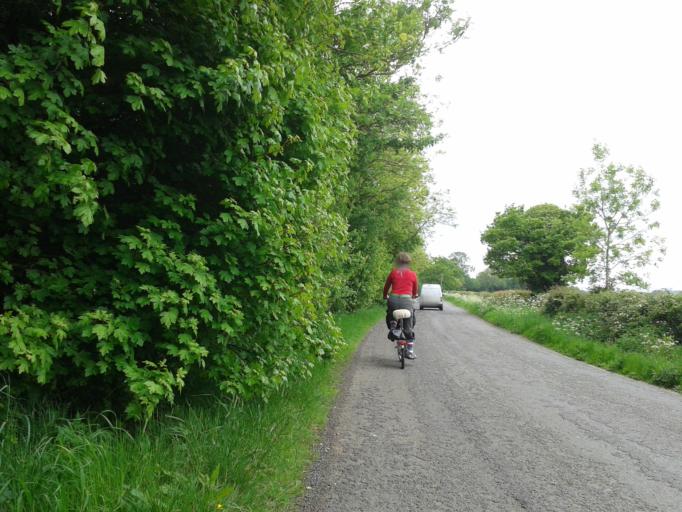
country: GB
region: England
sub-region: Northamptonshire
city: Corby
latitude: 52.5198
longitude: -0.6346
